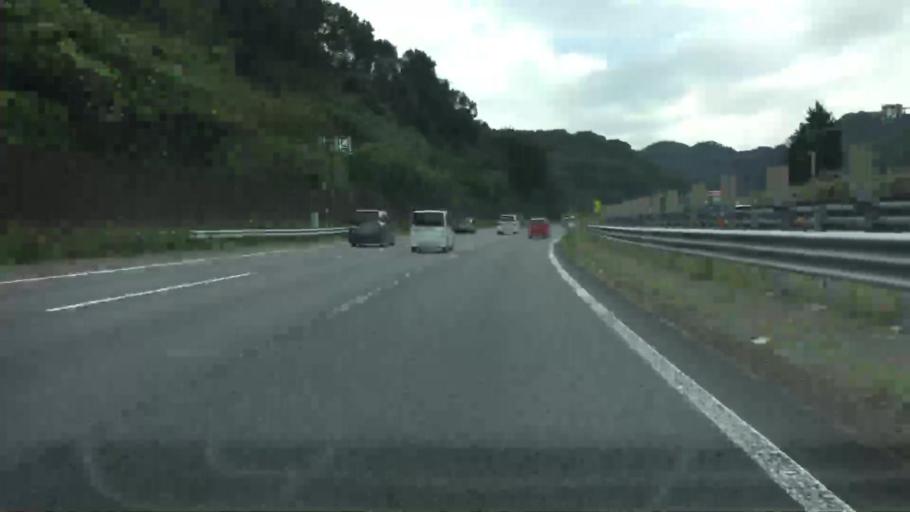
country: JP
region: Tochigi
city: Tochigi
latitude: 36.3834
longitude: 139.6697
